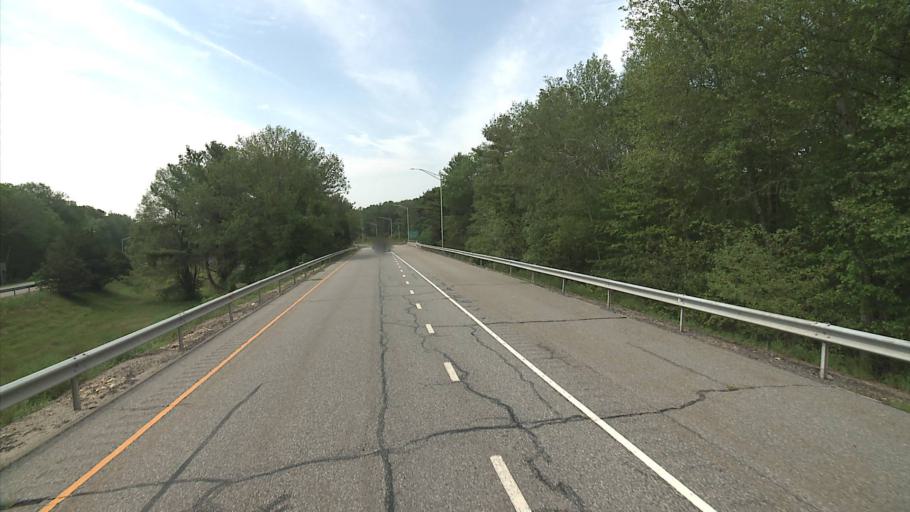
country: US
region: Connecticut
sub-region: Windham County
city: Danielson
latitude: 41.7657
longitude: -71.8708
